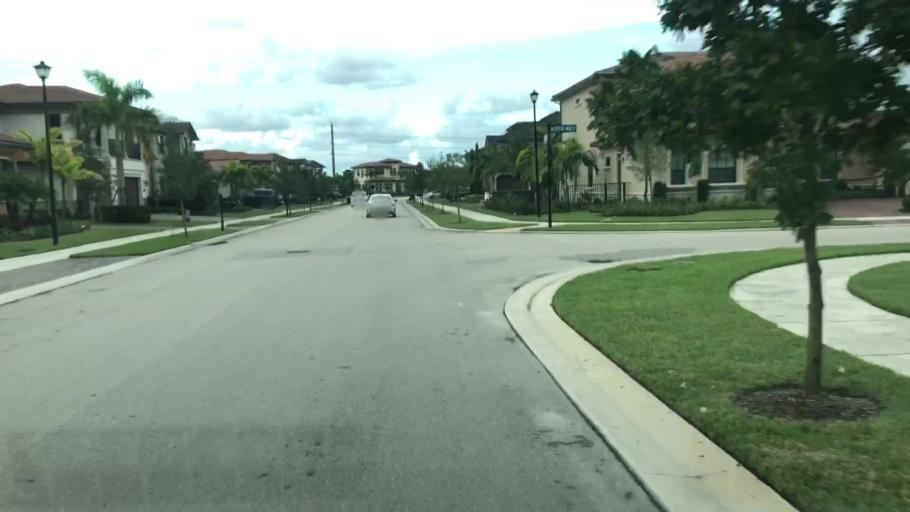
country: US
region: Florida
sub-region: Broward County
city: Parkland
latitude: 26.3450
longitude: -80.2778
